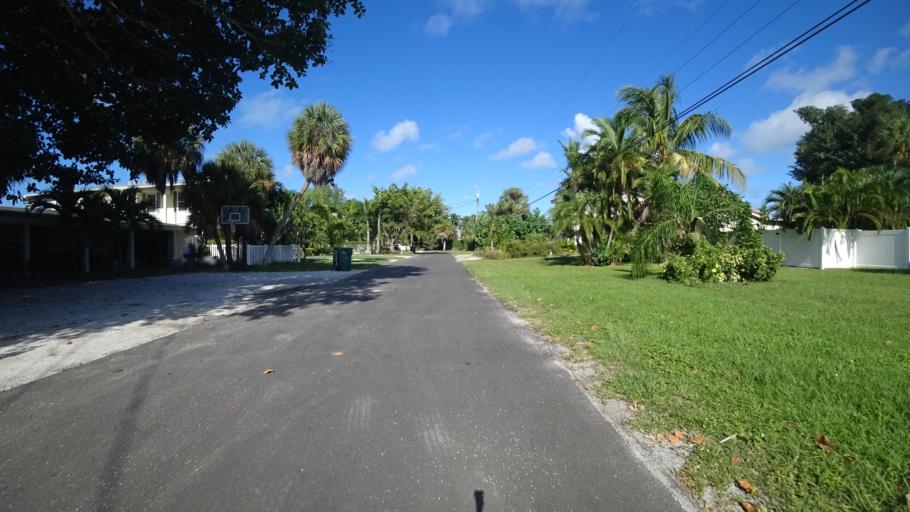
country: US
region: Florida
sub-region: Manatee County
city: Anna Maria
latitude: 27.5240
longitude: -82.7286
